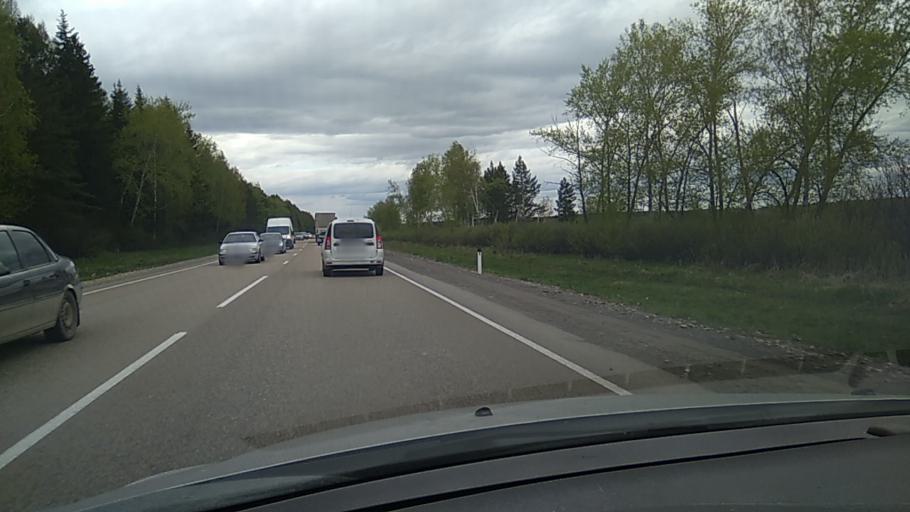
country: RU
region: Sverdlovsk
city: Dvurechensk
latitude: 56.6657
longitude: 61.1586
